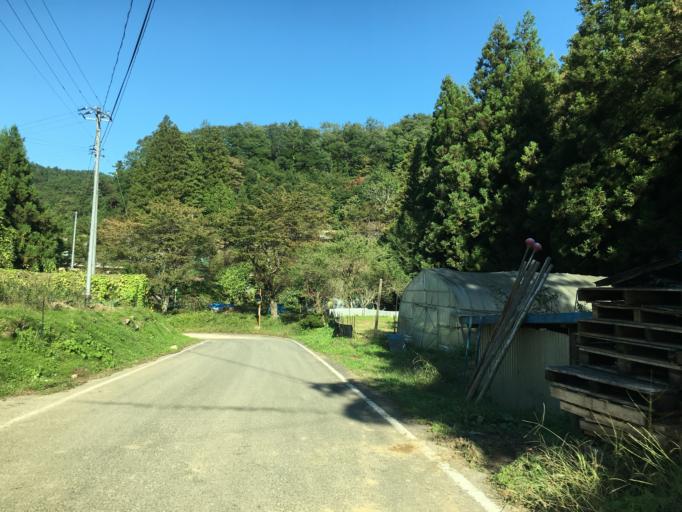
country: JP
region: Fukushima
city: Fukushima-shi
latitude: 37.6424
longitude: 140.6157
